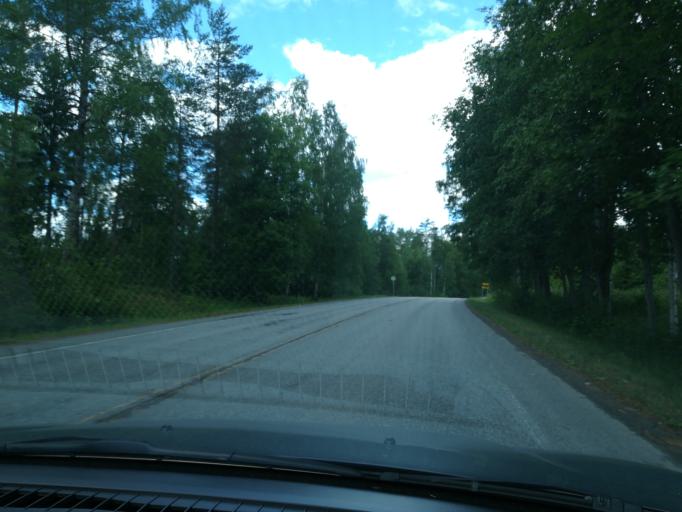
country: FI
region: Southern Savonia
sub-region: Mikkeli
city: Maentyharju
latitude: 61.4087
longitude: 26.8870
